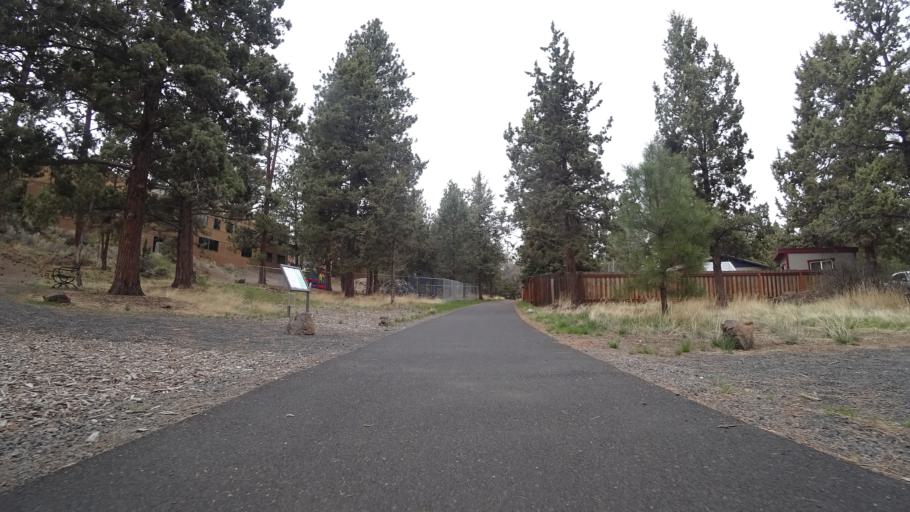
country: US
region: Oregon
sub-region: Deschutes County
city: Bend
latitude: 44.0523
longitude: -121.2912
